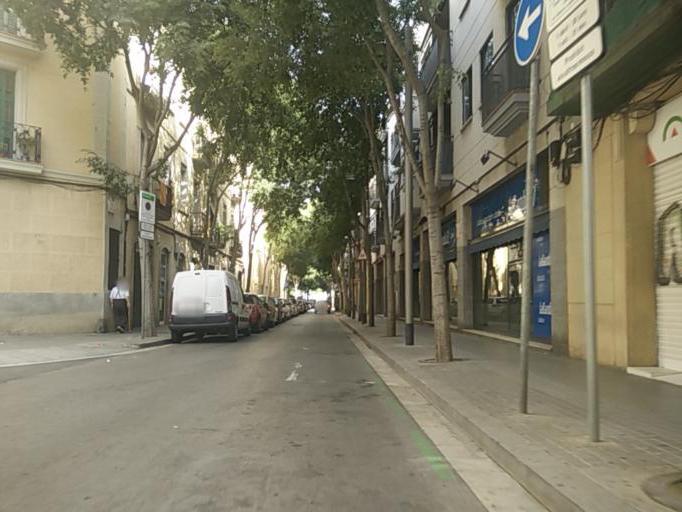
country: ES
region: Catalonia
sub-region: Provincia de Barcelona
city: Sants-Montjuic
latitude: 41.3773
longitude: 2.1439
